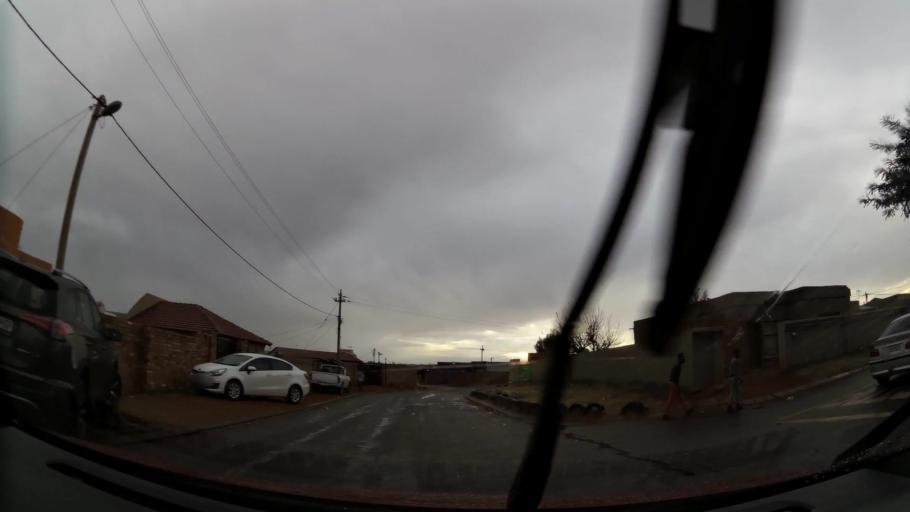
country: ZA
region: Gauteng
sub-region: West Rand District Municipality
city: Randfontein
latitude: -26.1764
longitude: 27.7815
